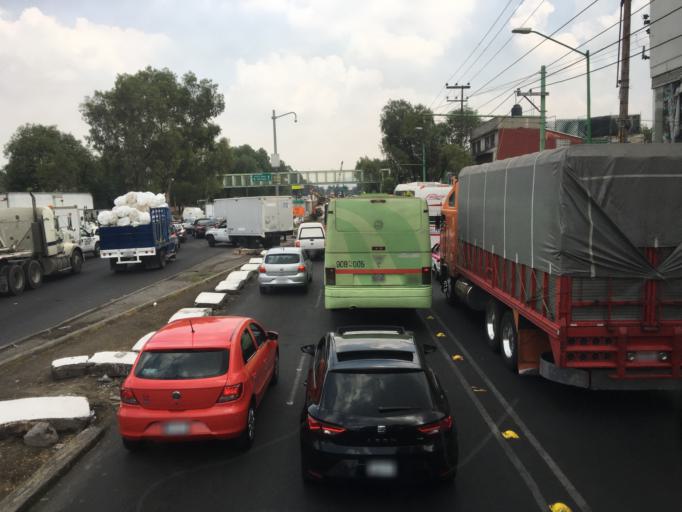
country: MX
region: Mexico
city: Colonia Lindavista
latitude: 19.4907
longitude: -99.1448
